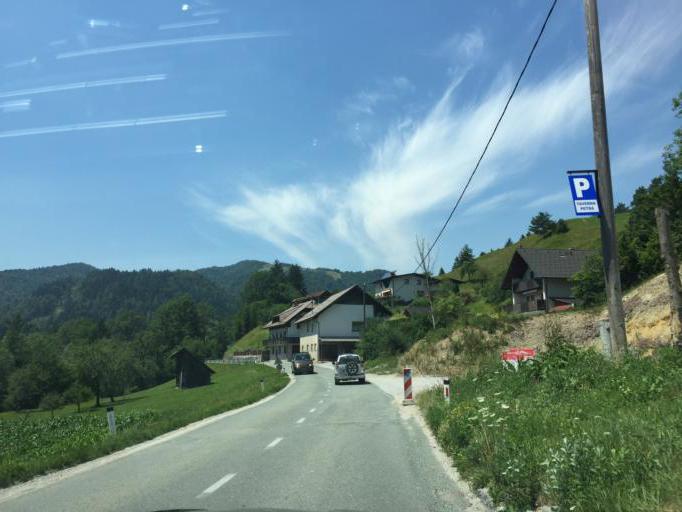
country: SI
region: Gorenja Vas-Poljane
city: Gorenja Vas
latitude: 46.1066
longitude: 14.1300
